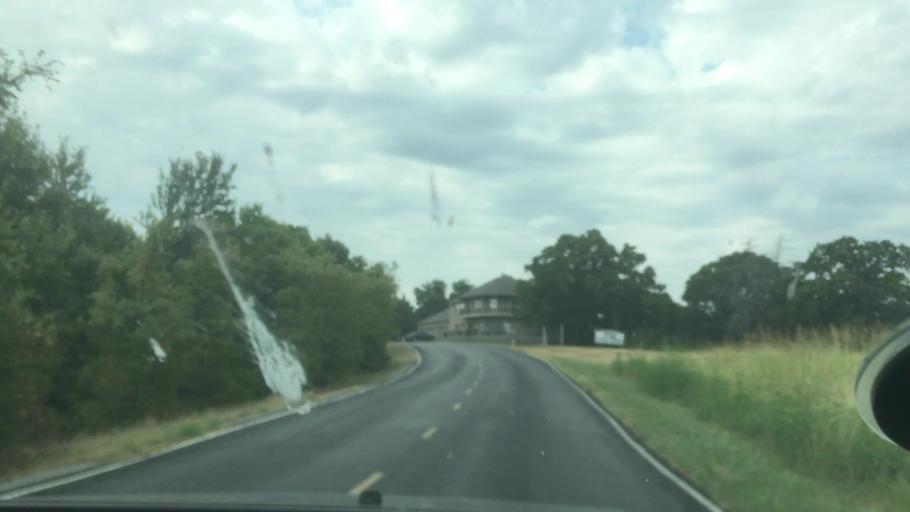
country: US
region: Texas
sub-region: Grayson County
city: Pottsboro
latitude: 33.8173
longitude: -96.7078
